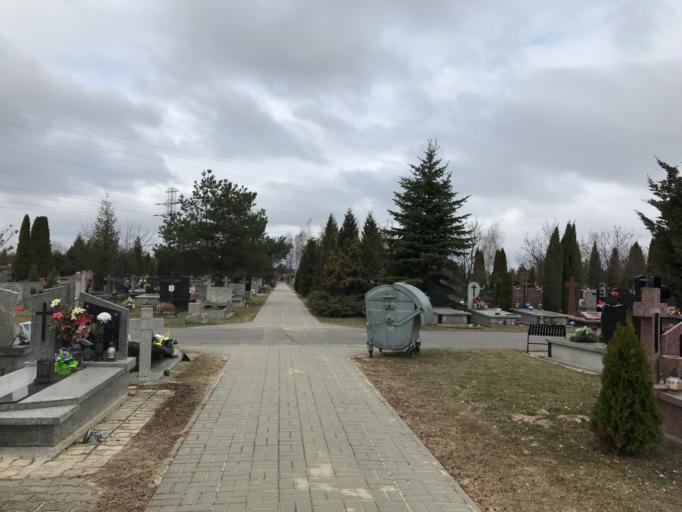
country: PL
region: Masovian Voivodeship
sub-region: Powiat warszawski zachodni
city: Lomianki
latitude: 52.3016
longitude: 20.8889
